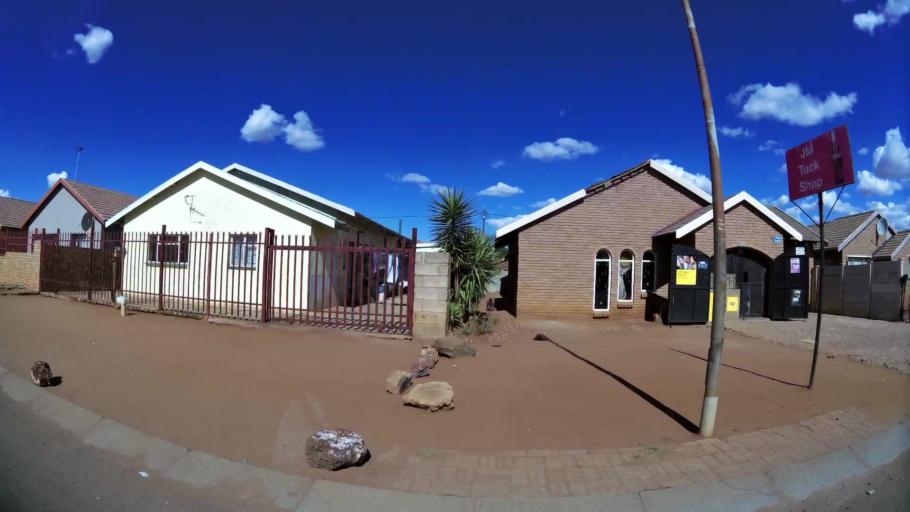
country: ZA
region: North-West
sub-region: Dr Kenneth Kaunda District Municipality
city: Klerksdorp
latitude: -26.8687
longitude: 26.5859
